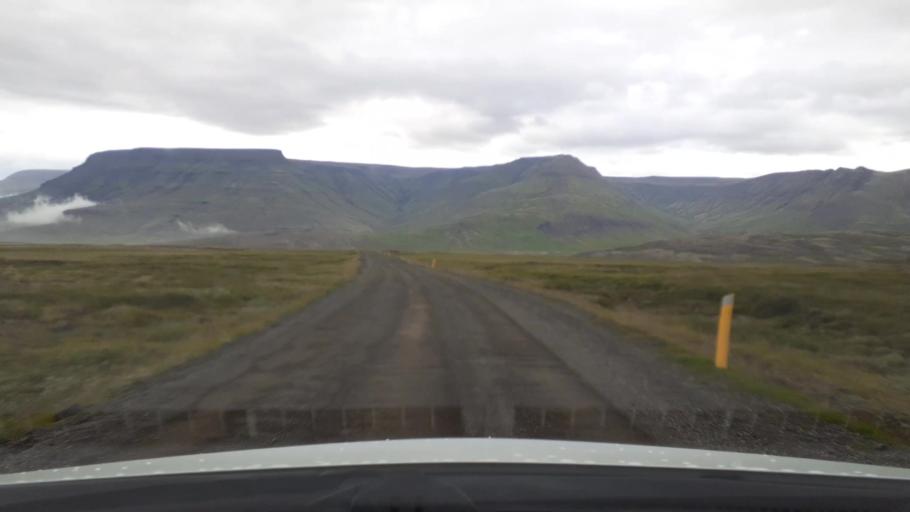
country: IS
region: Capital Region
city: Mosfellsbaer
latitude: 64.1932
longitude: -21.5426
